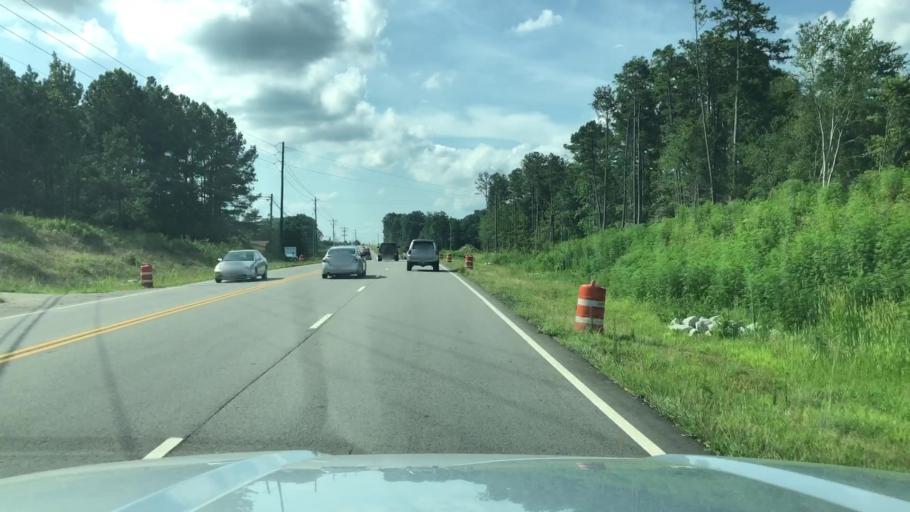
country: US
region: Georgia
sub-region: Douglas County
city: Douglasville
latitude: 33.7914
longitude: -84.7522
